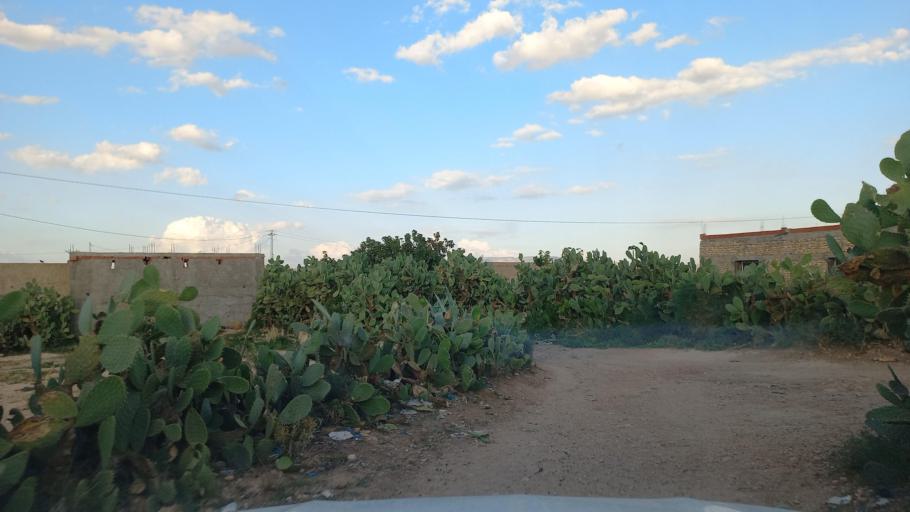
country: TN
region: Al Qasrayn
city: Sbiba
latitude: 35.3759
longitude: 9.0561
